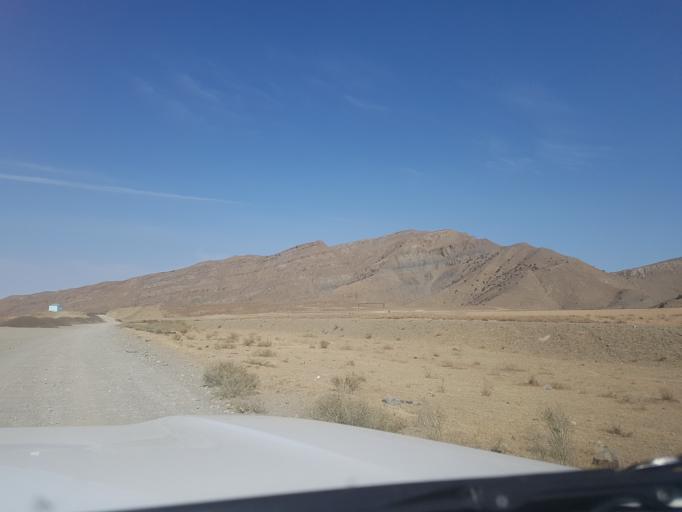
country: TM
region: Ahal
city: Baharly
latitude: 38.4410
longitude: 57.0416
